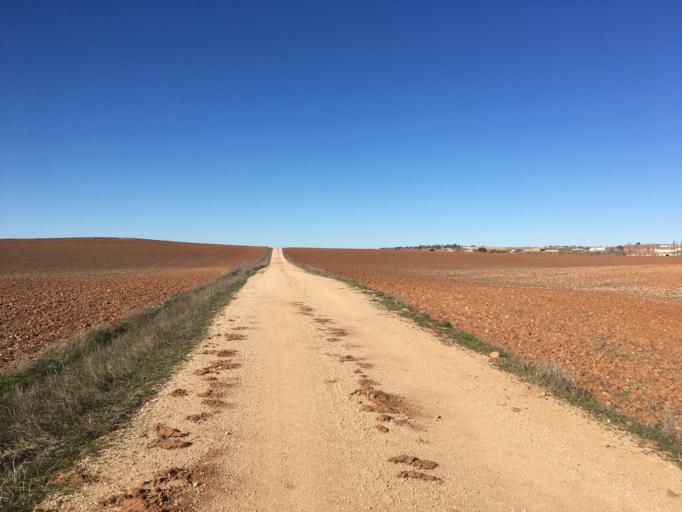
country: ES
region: Castille-La Mancha
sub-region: Provincia de Cuenca
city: Atalaya del Canavate
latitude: 39.5405
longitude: -2.2411
